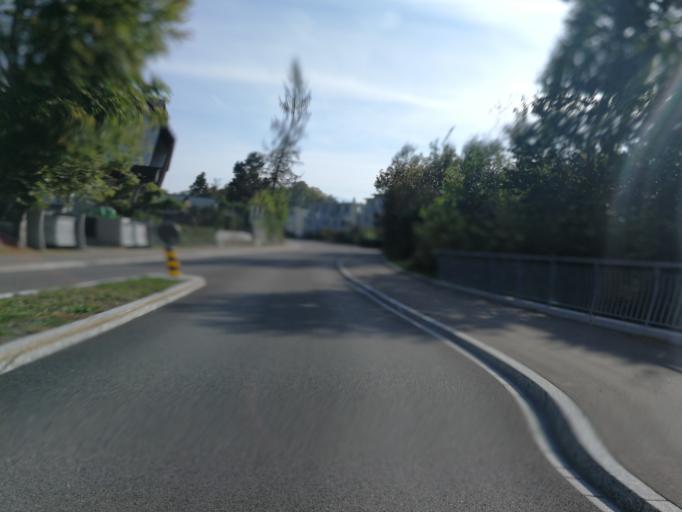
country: CH
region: Zurich
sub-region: Bezirk Hinwil
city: Hadlikon
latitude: 47.2775
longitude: 8.8708
